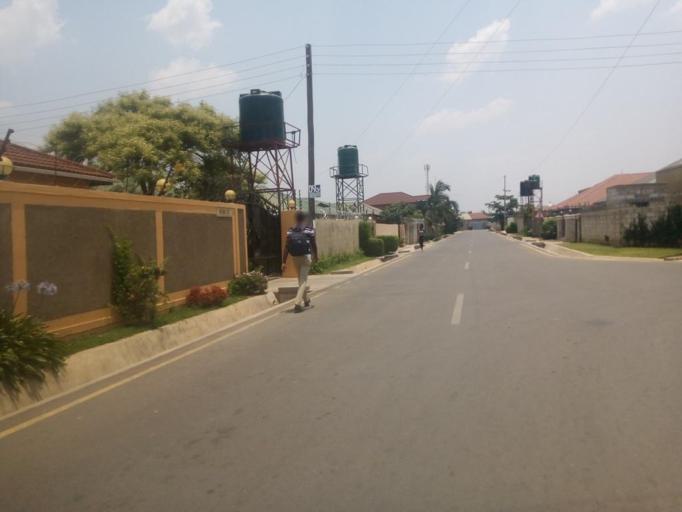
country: ZM
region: Lusaka
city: Lusaka
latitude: -15.3986
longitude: 28.3920
